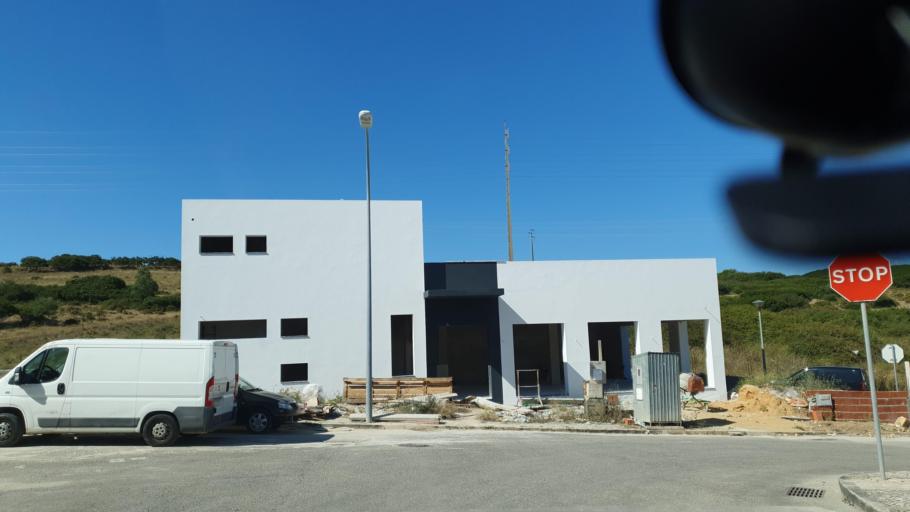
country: PT
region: Lisbon
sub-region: Odivelas
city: Canecas
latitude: 38.8062
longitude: -9.2538
